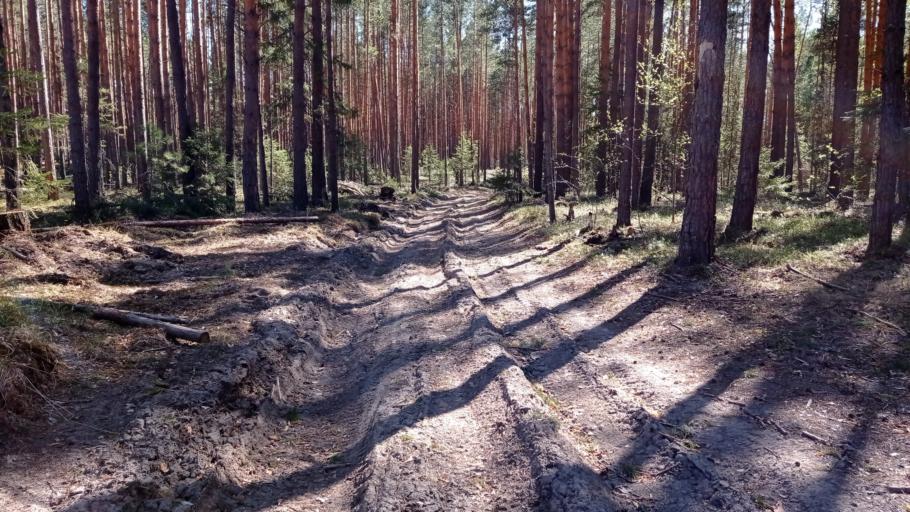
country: RU
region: Tomsk
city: Timiryazevskoye
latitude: 56.4265
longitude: 84.7615
